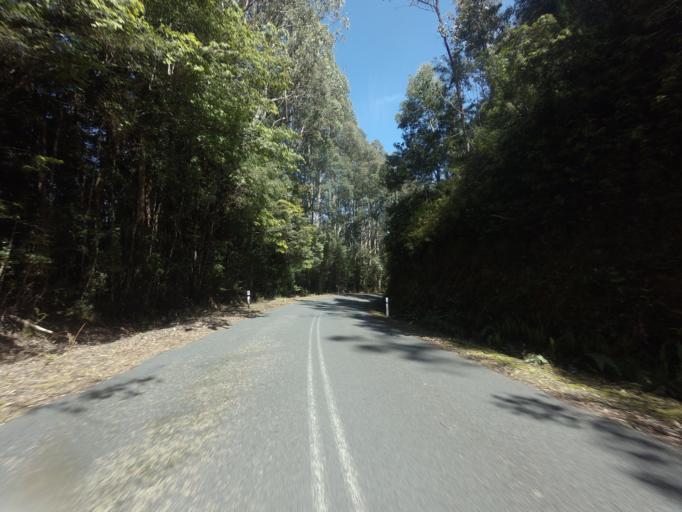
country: AU
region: Tasmania
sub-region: Huon Valley
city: Geeveston
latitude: -42.8204
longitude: 146.3408
